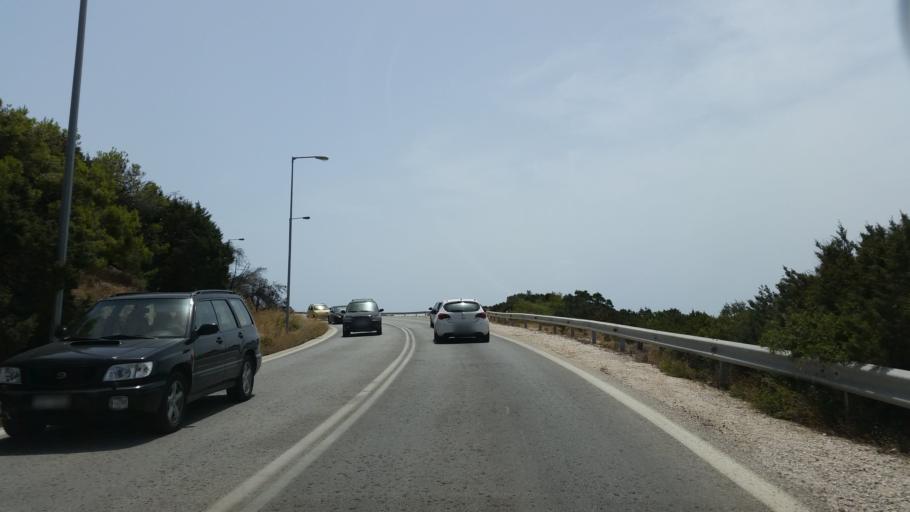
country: GR
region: Attica
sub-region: Nomarchia Anatolikis Attikis
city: Palaia Fokaia
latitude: 37.6888
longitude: 23.9385
